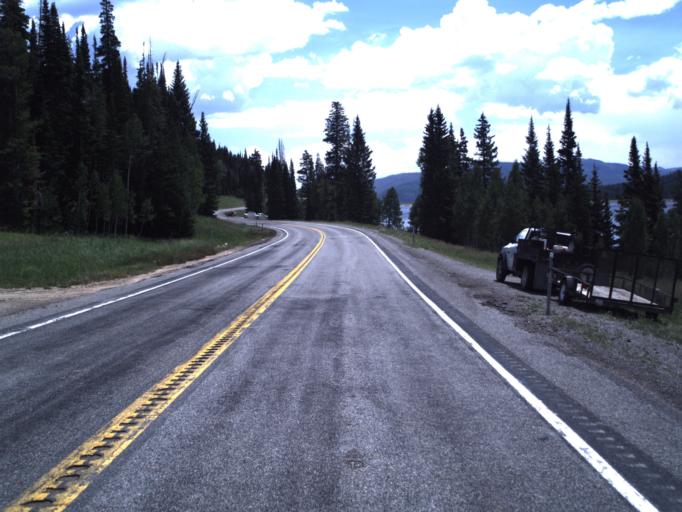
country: US
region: Utah
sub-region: Sanpete County
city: Fairview
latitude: 39.5943
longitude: -111.2676
